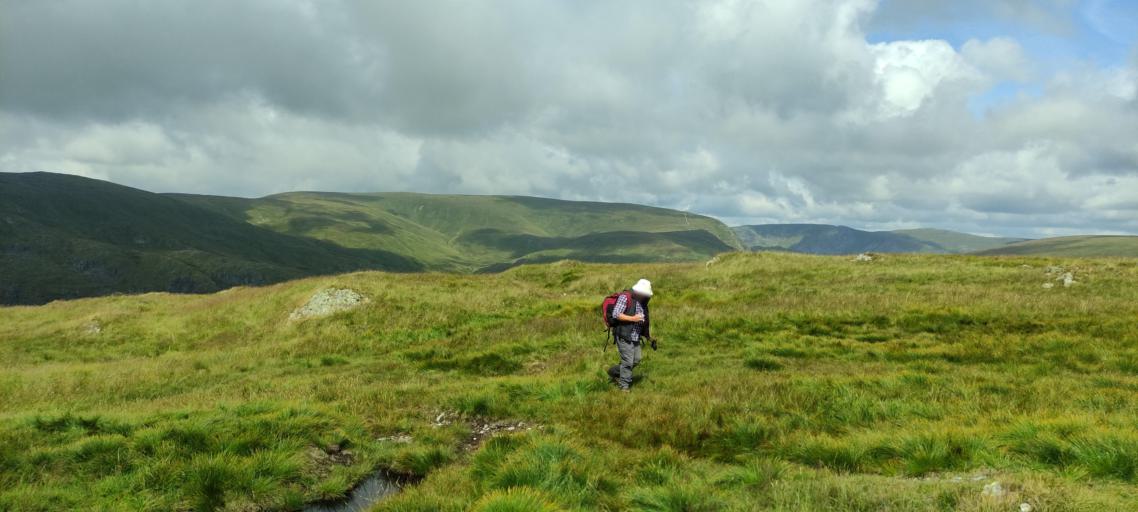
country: GB
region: England
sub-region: Cumbria
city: Windermere
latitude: 54.4631
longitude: -2.7914
